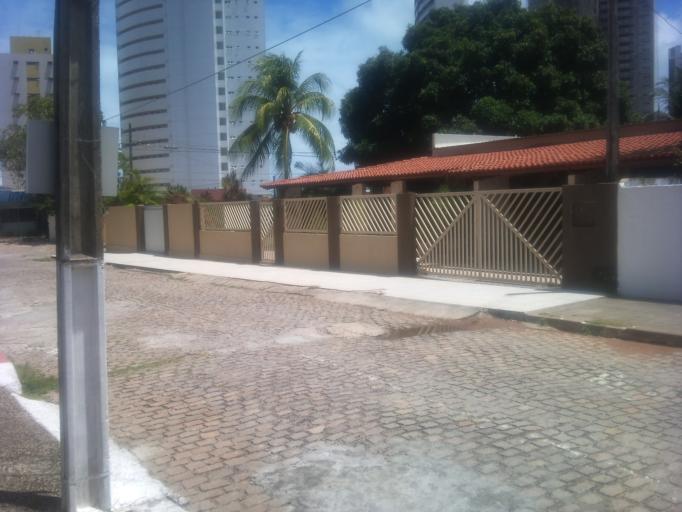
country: BR
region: Rio Grande do Norte
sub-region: Natal
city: Natal
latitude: -5.8783
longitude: -35.1787
